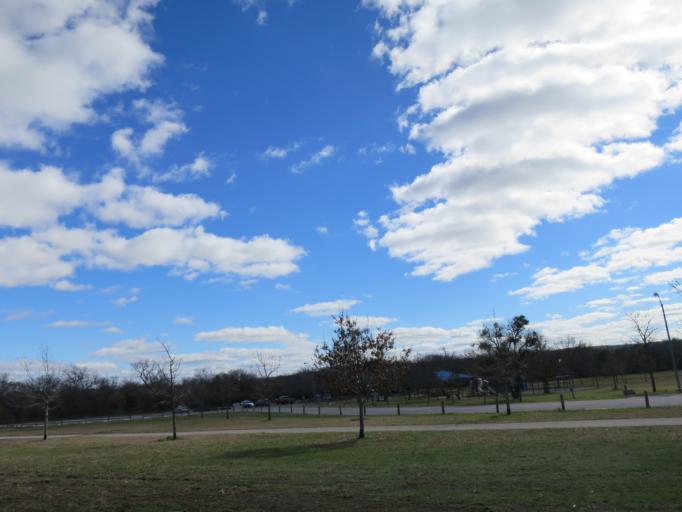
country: US
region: Texas
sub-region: Williamson County
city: Round Rock
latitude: 30.5349
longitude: -97.6270
